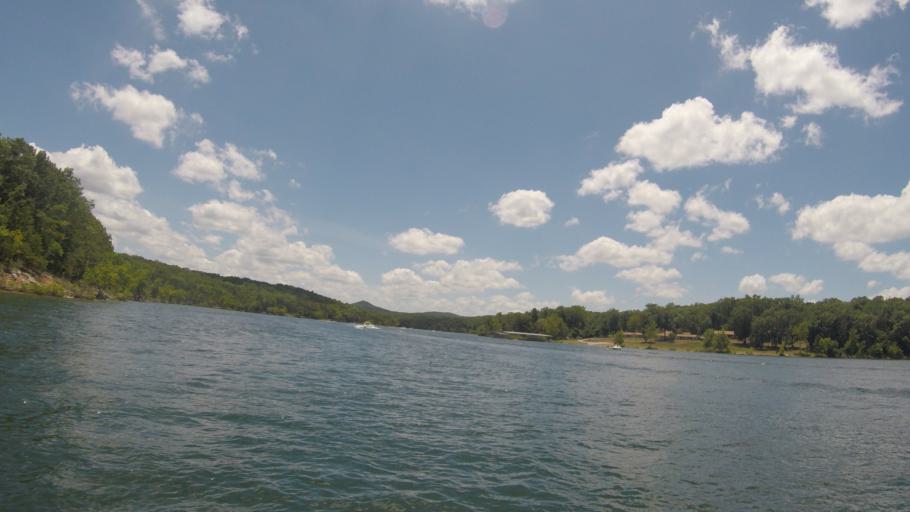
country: US
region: Missouri
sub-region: Barry County
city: Shell Knob
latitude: 36.5827
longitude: -93.5672
